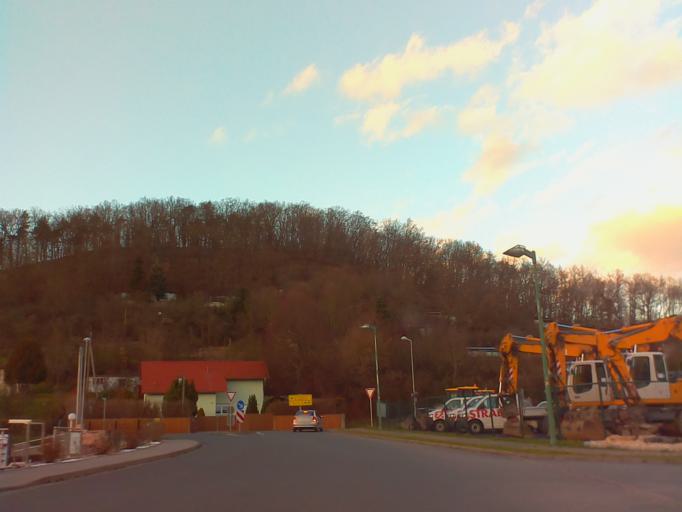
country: DE
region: Thuringia
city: Rudolstadt
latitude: 50.7277
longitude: 11.3714
